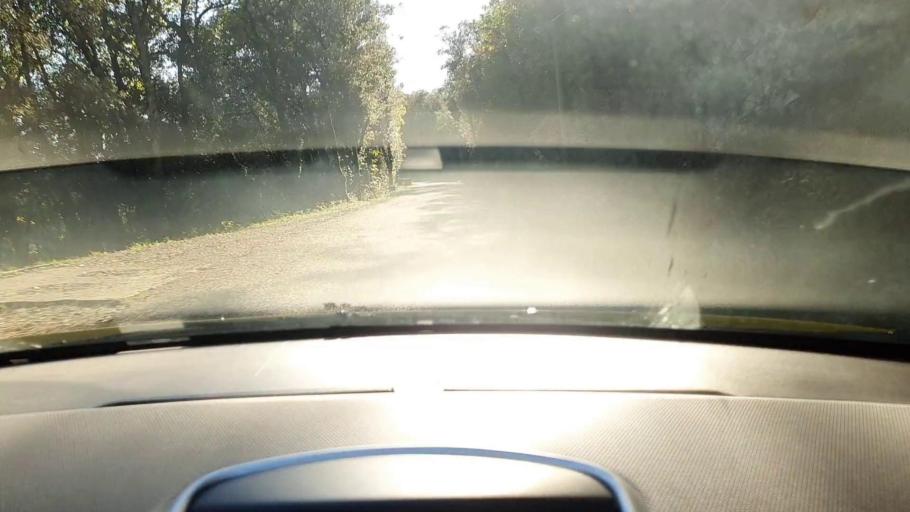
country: FR
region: Languedoc-Roussillon
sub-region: Departement du Gard
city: Sumene
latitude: 43.9848
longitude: 3.6824
